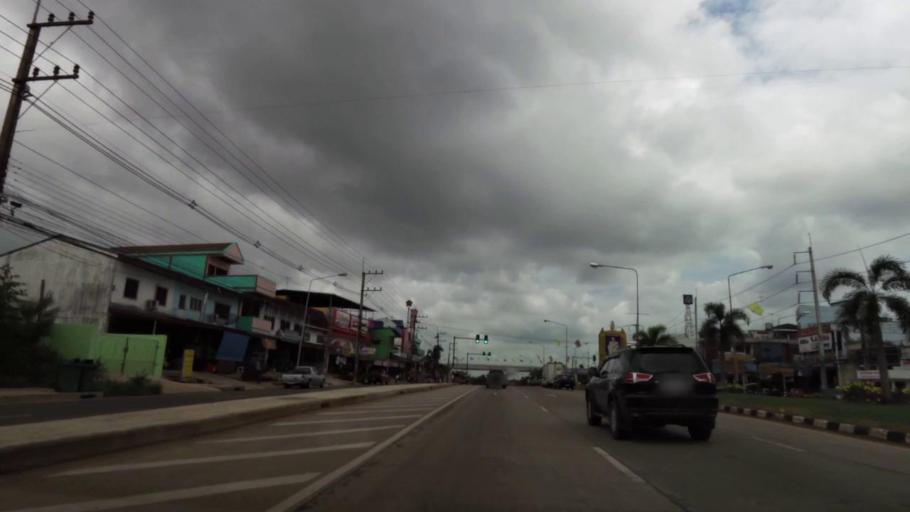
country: TH
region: Chanthaburi
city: Na Yai Am
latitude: 12.7791
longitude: 101.8235
